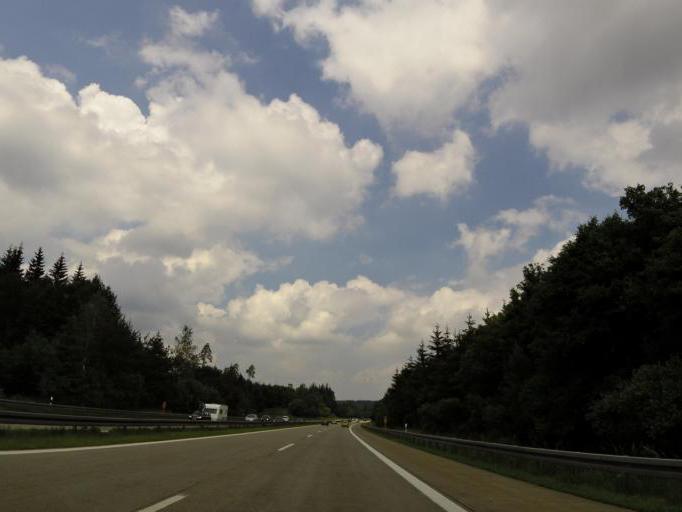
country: DE
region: Baden-Wuerttemberg
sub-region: Regierungsbezirk Stuttgart
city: Ellenberg
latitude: 49.0018
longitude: 10.1930
